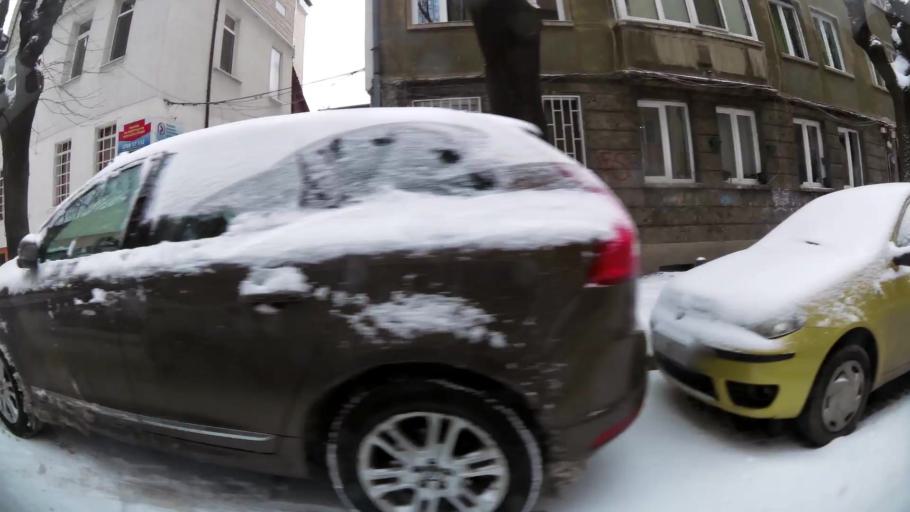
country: BG
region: Sofia-Capital
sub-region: Stolichna Obshtina
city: Sofia
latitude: 42.6921
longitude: 23.3128
